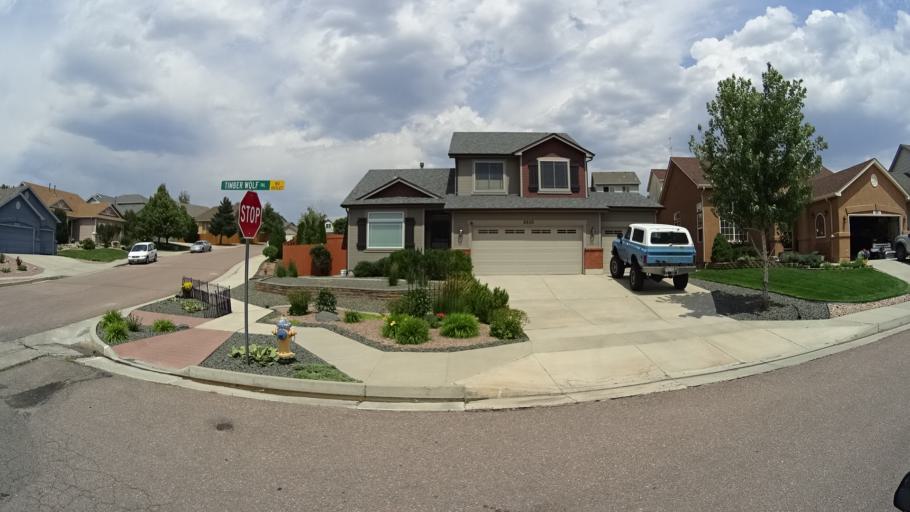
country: US
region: Colorado
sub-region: El Paso County
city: Black Forest
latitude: 38.9636
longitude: -104.7401
